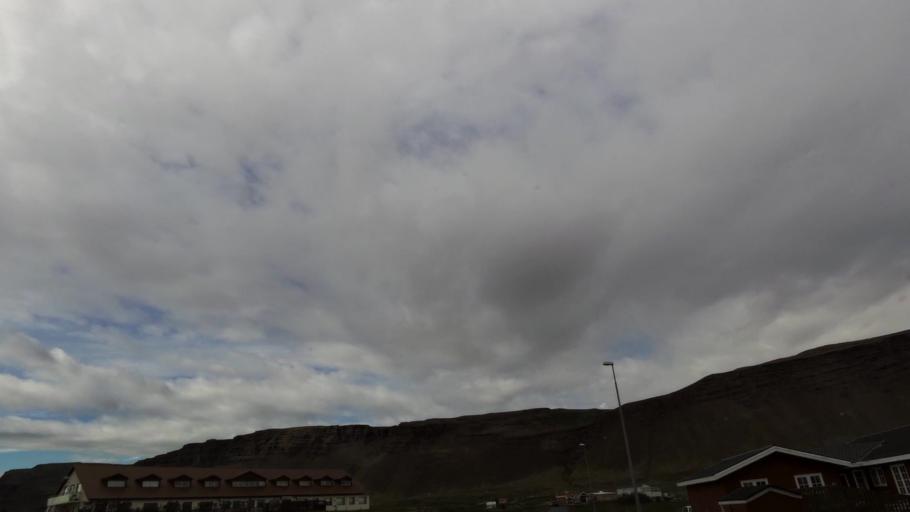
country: IS
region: West
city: Stykkisholmur
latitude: 65.4490
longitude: -22.2005
